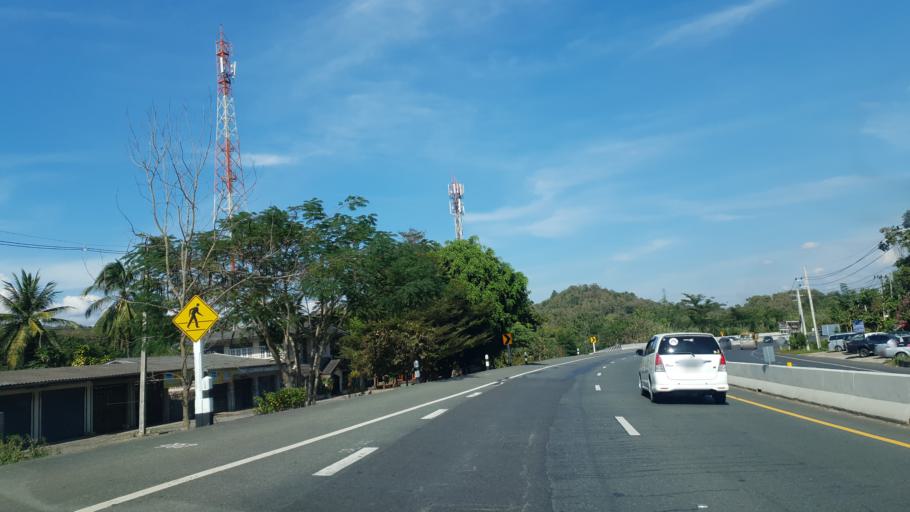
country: TH
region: Phrae
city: Den Chai
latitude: 17.8928
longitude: 100.0484
